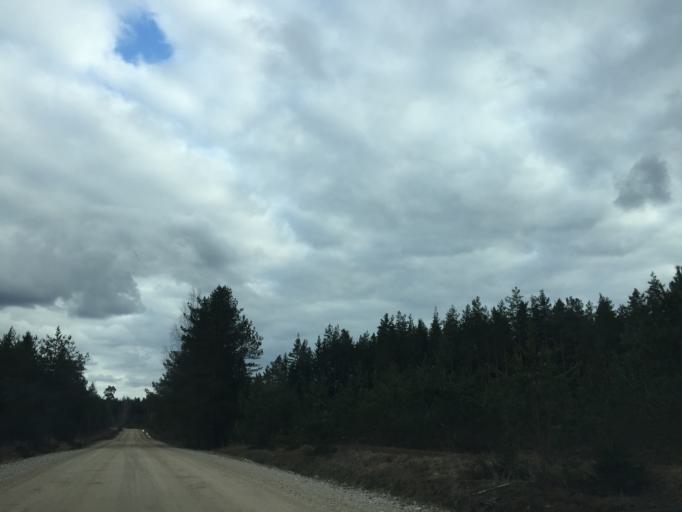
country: LV
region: Ogre
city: Jumprava
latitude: 56.5899
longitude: 24.9910
